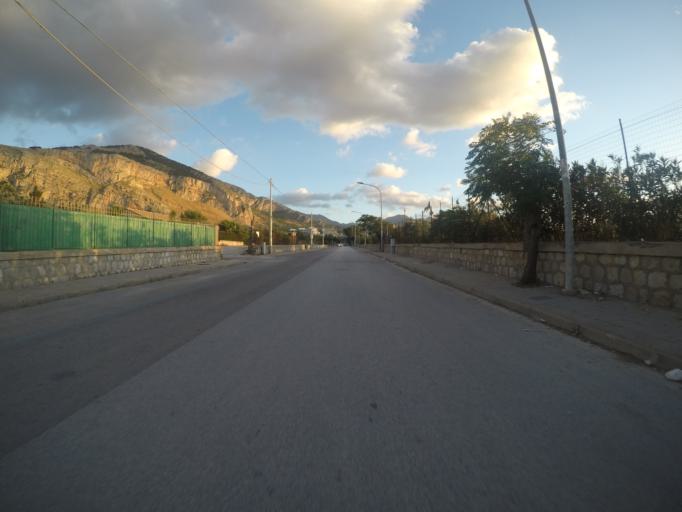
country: IT
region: Sicily
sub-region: Palermo
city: Isola delle Femmine
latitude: 38.1842
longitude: 13.2380
